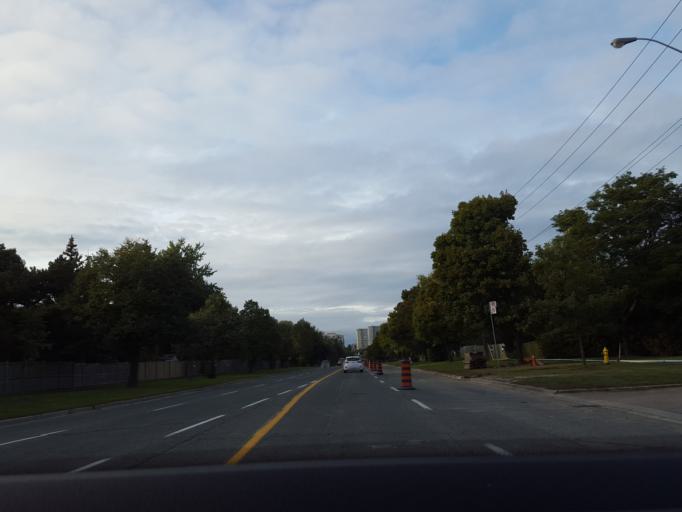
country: CA
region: Ontario
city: Scarborough
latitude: 43.7859
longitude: -79.3110
